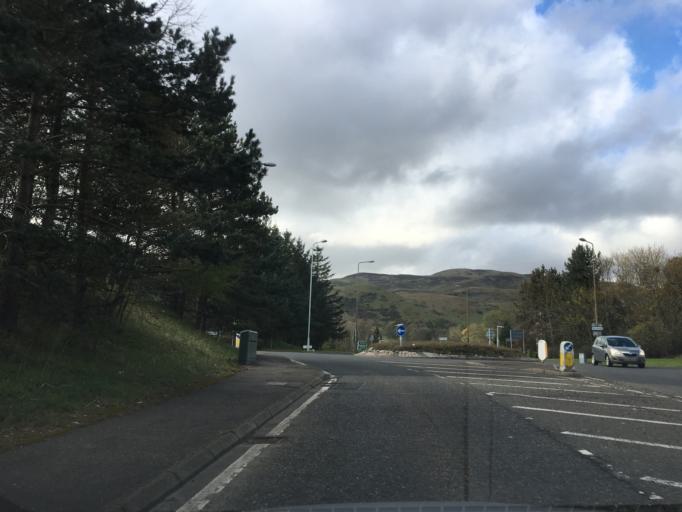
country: GB
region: Scotland
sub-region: Edinburgh
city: Colinton
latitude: 55.9008
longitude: -3.2309
